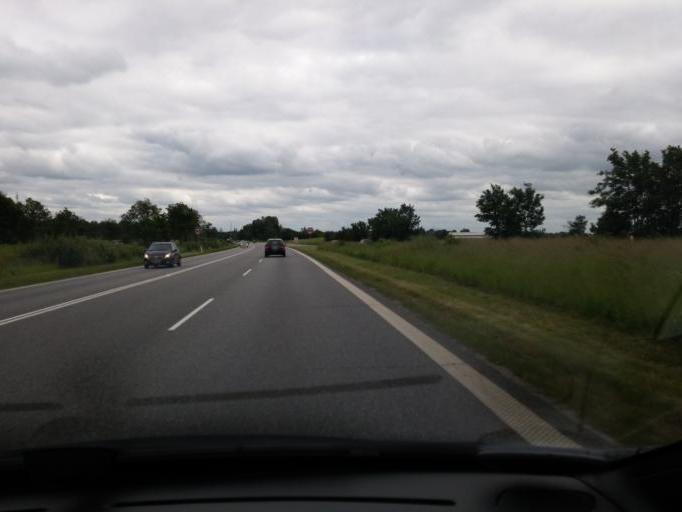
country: DK
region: Capital Region
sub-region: Hillerod Kommune
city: Hillerod
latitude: 55.9050
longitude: 12.2694
